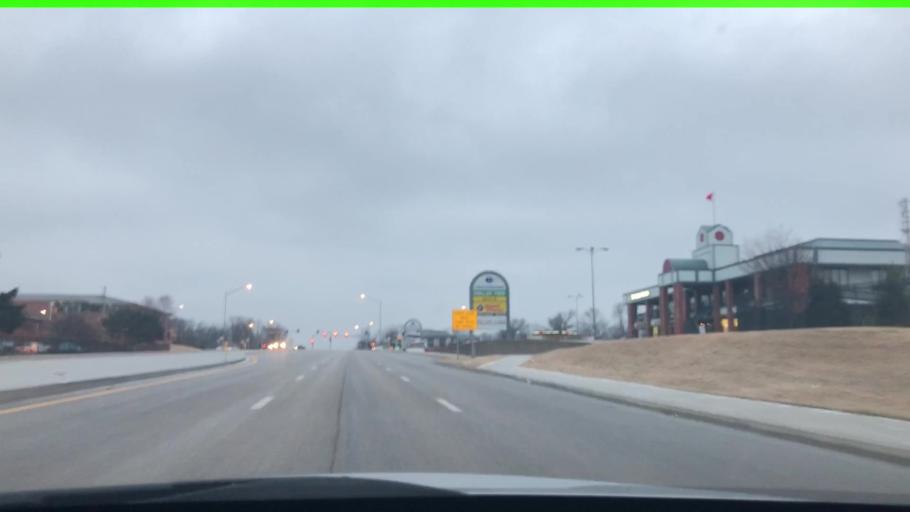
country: US
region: Missouri
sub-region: Boone County
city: Columbia
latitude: 38.9564
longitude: -92.3715
